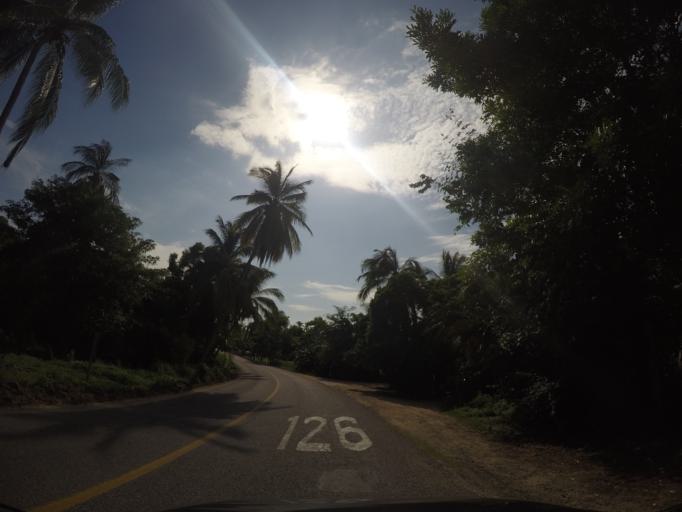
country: MX
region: Oaxaca
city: San Pedro Mixtepec
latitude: 15.9399
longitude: -97.1600
